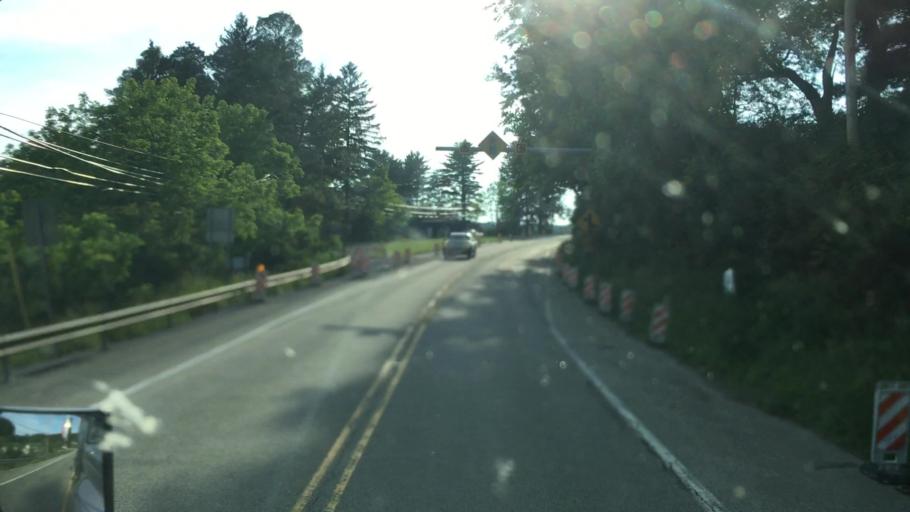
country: US
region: Pennsylvania
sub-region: Fayette County
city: Hopwood
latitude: 39.8058
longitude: -79.5619
